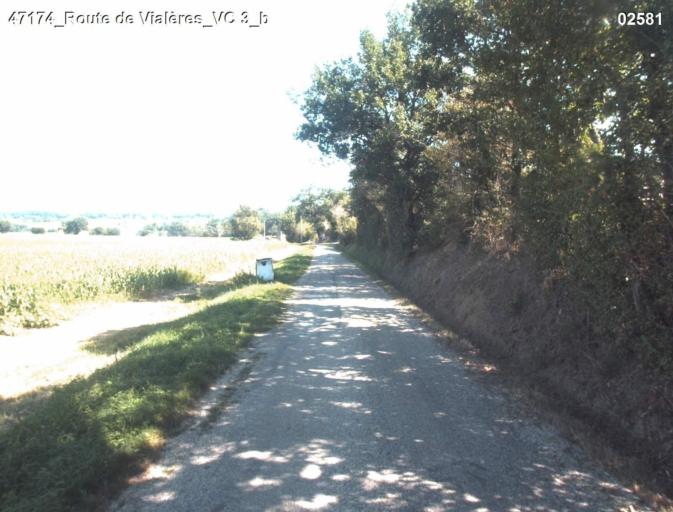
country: FR
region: Aquitaine
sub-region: Departement du Lot-et-Garonne
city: Nerac
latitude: 44.0555
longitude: 0.3849
